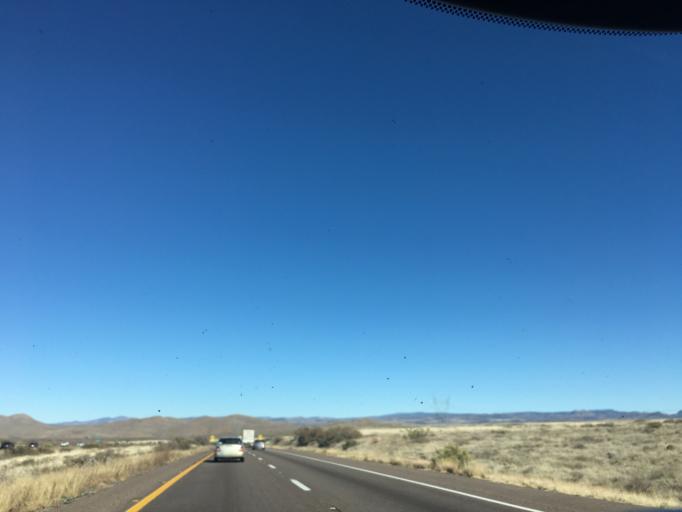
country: US
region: Arizona
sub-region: Yavapai County
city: Cordes Lakes
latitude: 34.2092
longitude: -112.1171
